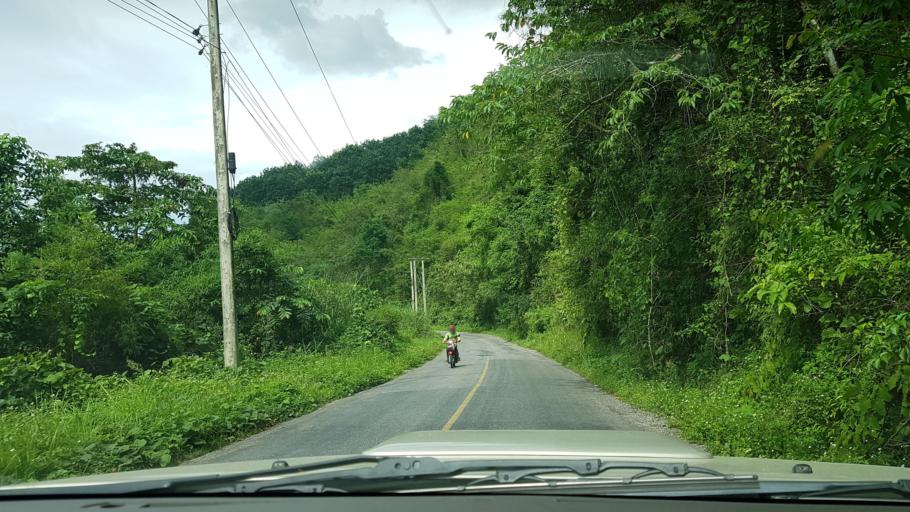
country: LA
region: Loungnamtha
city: Muang Nale
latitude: 20.3707
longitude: 101.7227
